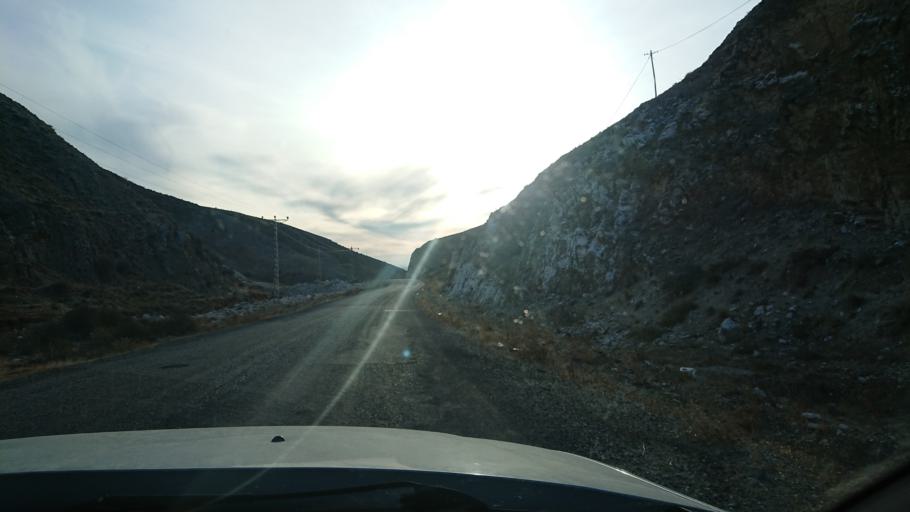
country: TR
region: Ankara
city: Sereflikochisar
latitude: 38.7519
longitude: 33.6912
